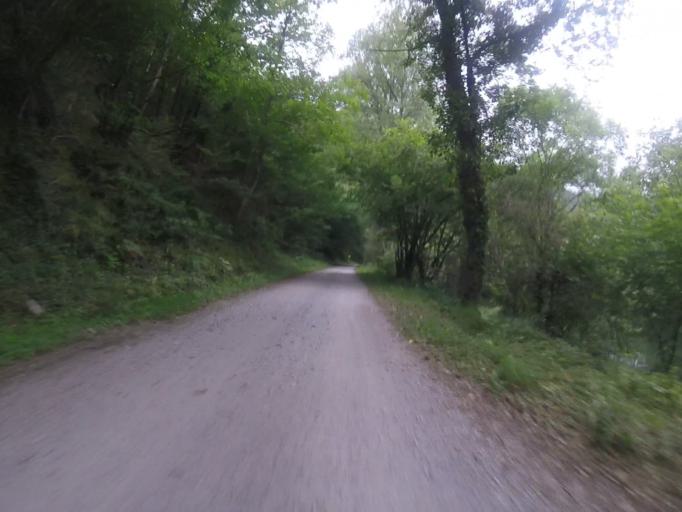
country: ES
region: Navarre
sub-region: Provincia de Navarra
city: Igantzi
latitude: 43.2114
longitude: -1.6712
